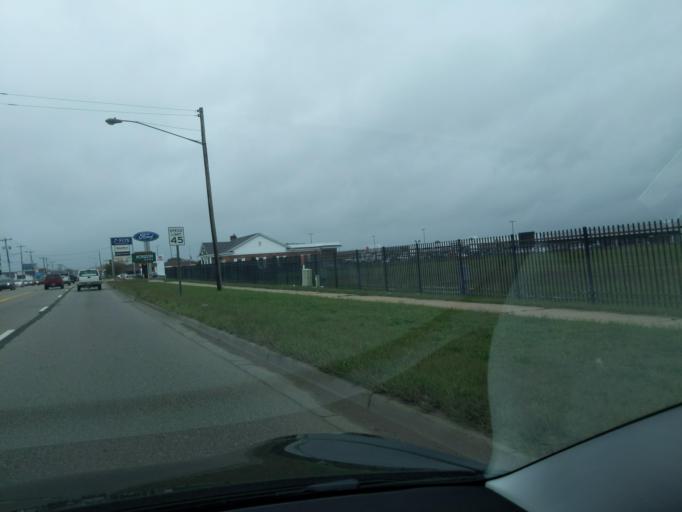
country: US
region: Michigan
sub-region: Wexford County
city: Cadillac
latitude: 44.2697
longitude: -85.4064
